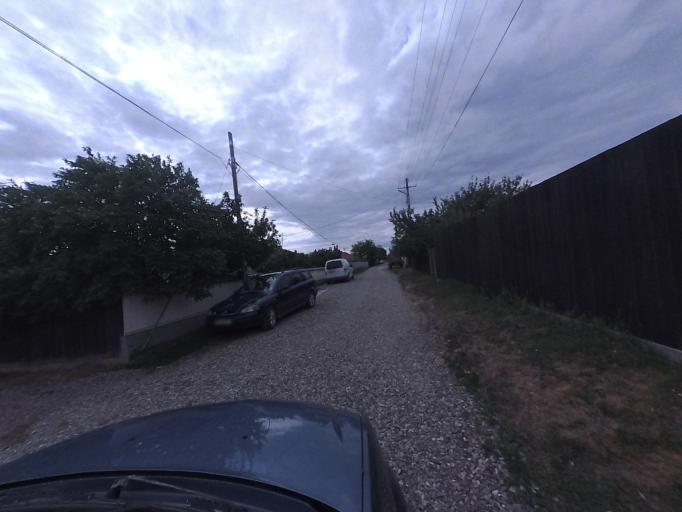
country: RO
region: Neamt
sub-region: Comuna Dulcesti
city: Dulcesti
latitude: 46.9597
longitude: 26.7970
